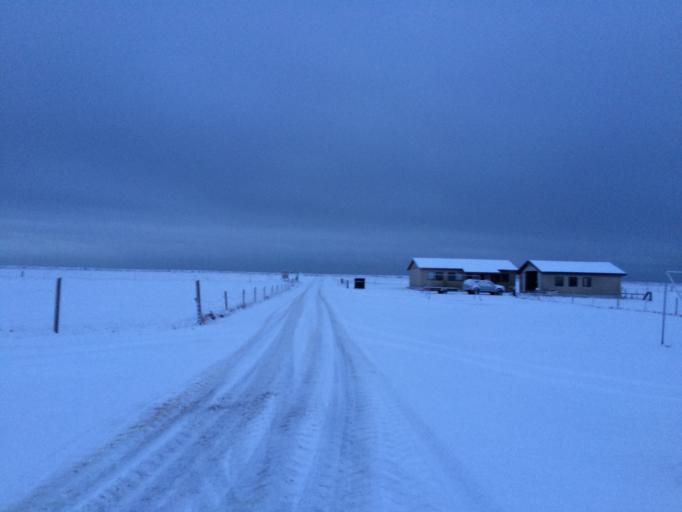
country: IS
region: South
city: Selfoss
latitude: 63.8310
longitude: -21.0210
